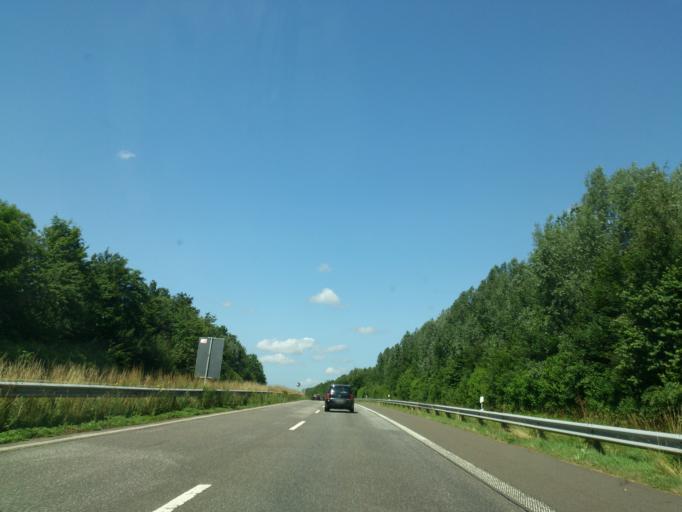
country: DE
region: Schleswig-Holstein
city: Arkebek
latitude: 54.1521
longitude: 9.2366
